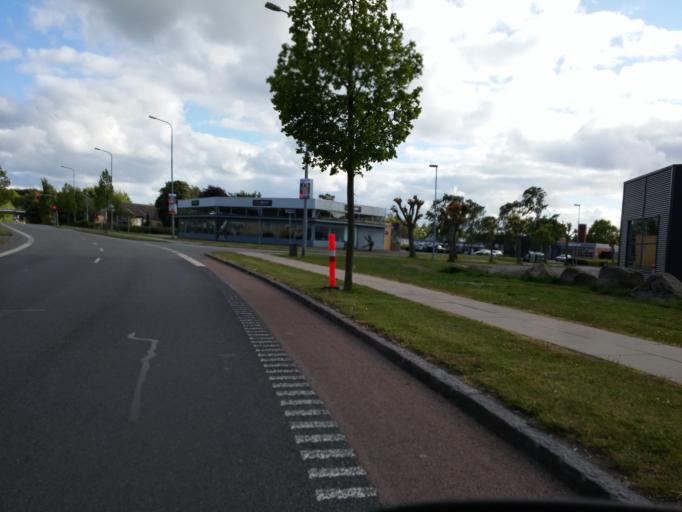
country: DK
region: South Denmark
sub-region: Kerteminde Kommune
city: Munkebo
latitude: 55.4554
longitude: 10.5493
